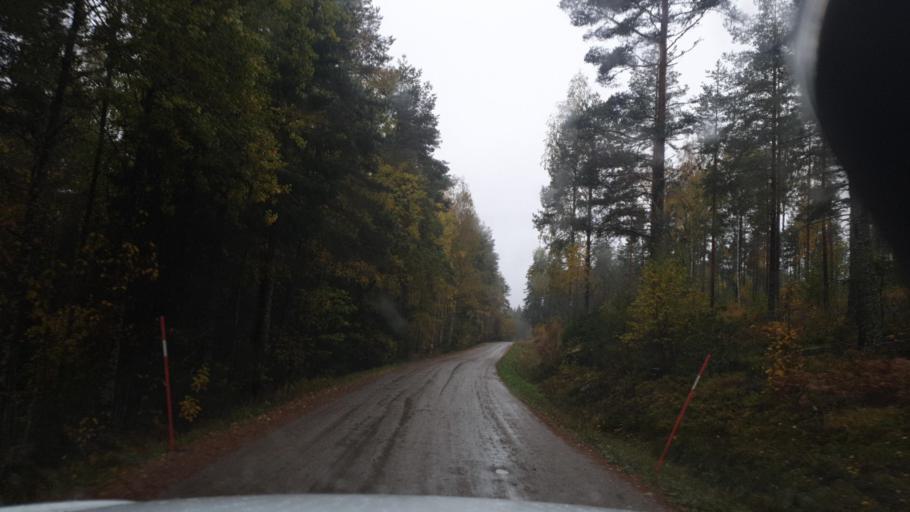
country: SE
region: Vaermland
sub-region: Eda Kommun
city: Amotfors
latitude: 59.7309
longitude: 12.2770
